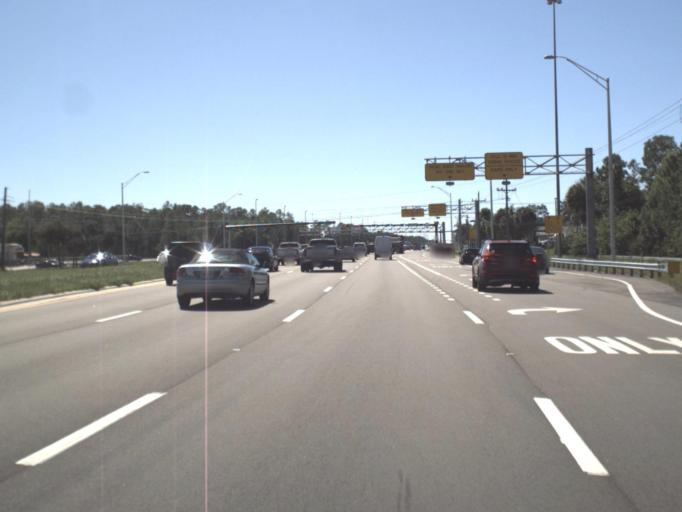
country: US
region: Florida
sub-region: Collier County
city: Golden Gate
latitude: 26.1570
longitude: -81.6867
